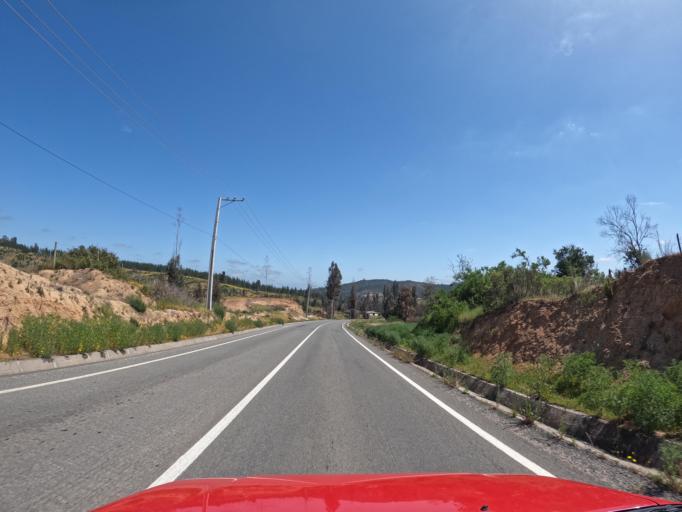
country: CL
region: O'Higgins
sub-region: Provincia de Colchagua
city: Santa Cruz
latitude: -34.6532
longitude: -71.8637
